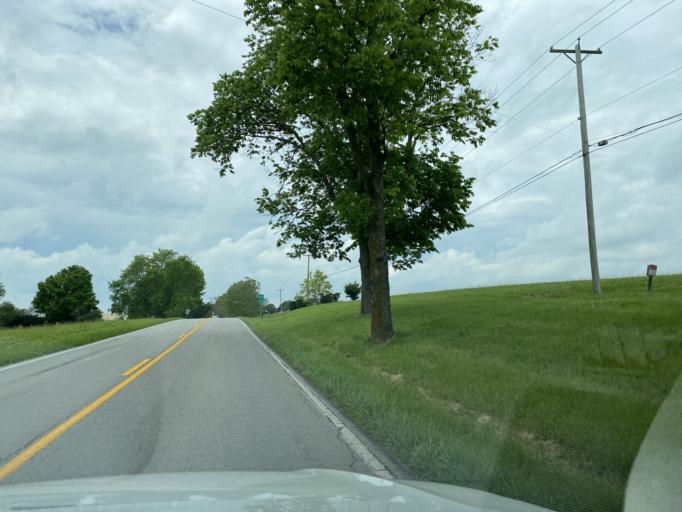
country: US
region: Kentucky
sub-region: Scott County
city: Georgetown
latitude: 38.2228
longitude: -84.4398
